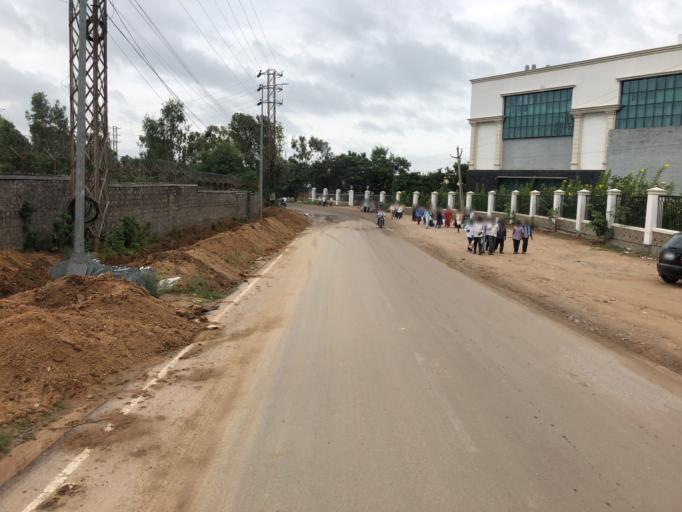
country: IN
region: Telangana
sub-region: Medak
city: Serilingampalle
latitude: 17.4444
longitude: 78.3054
